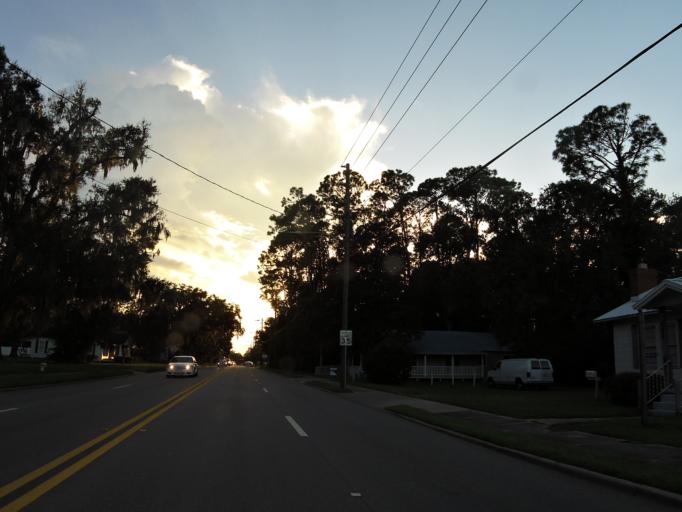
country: US
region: Georgia
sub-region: Camden County
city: Kingsland
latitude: 30.8009
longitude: -81.6845
